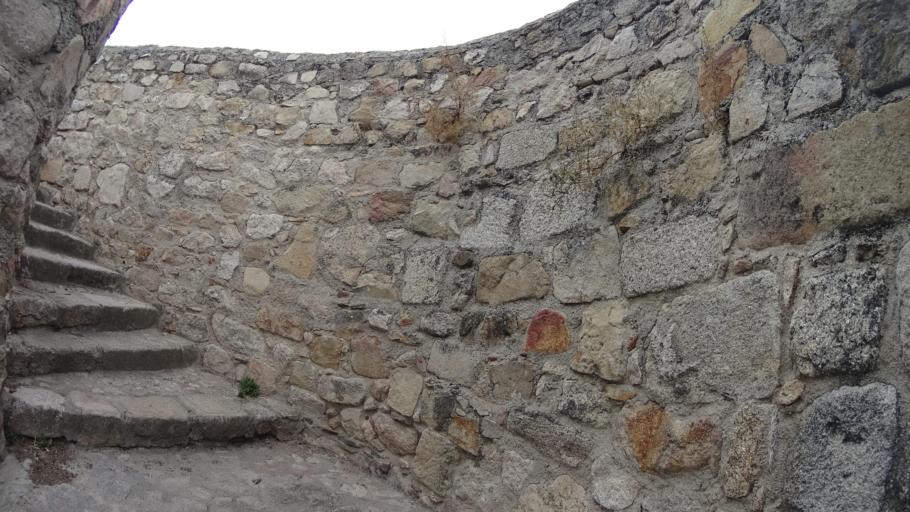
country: ES
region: Extremadura
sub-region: Provincia de Caceres
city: Trujillo
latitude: 39.4614
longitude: -5.8827
